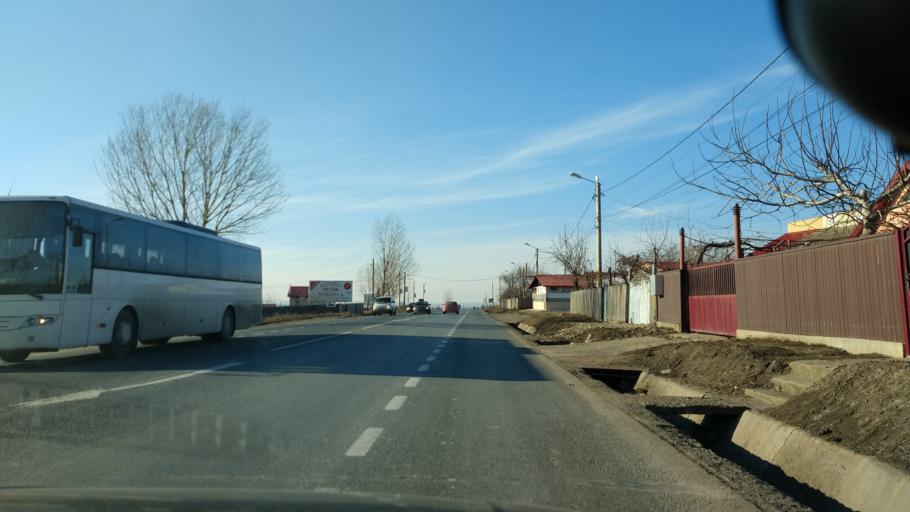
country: RO
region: Iasi
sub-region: Comuna Baltati
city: Baltati
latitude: 47.2188
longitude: 27.1156
